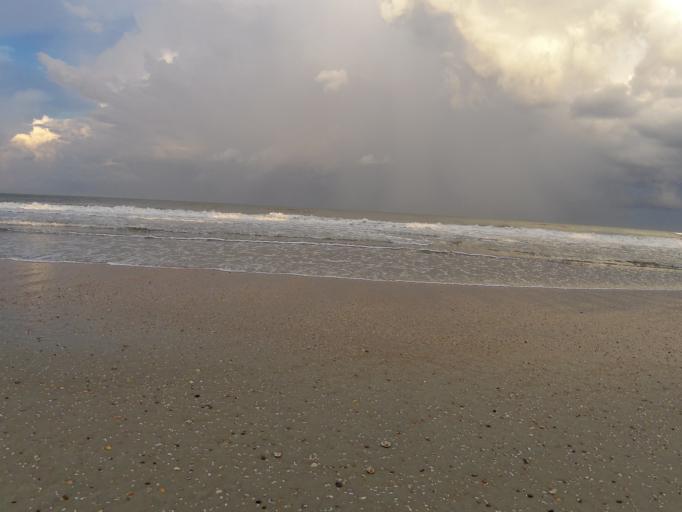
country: US
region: Florida
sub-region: Saint Johns County
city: Villano Beach
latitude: 29.9584
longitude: -81.3058
